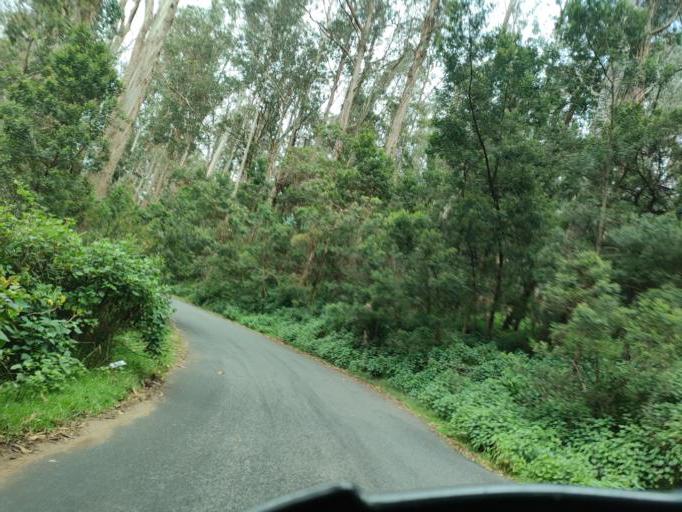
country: IN
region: Tamil Nadu
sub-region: Dindigul
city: Kodaikanal
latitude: 10.2417
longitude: 77.3720
